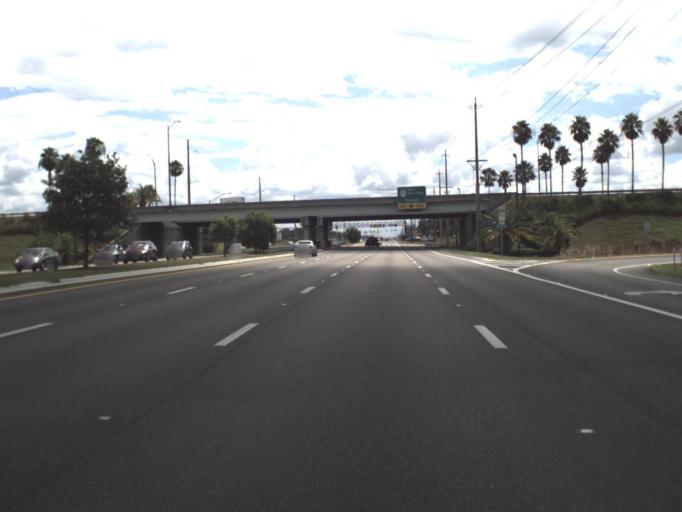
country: US
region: Florida
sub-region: Polk County
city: Crystal Lake
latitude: 28.0019
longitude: -81.9029
